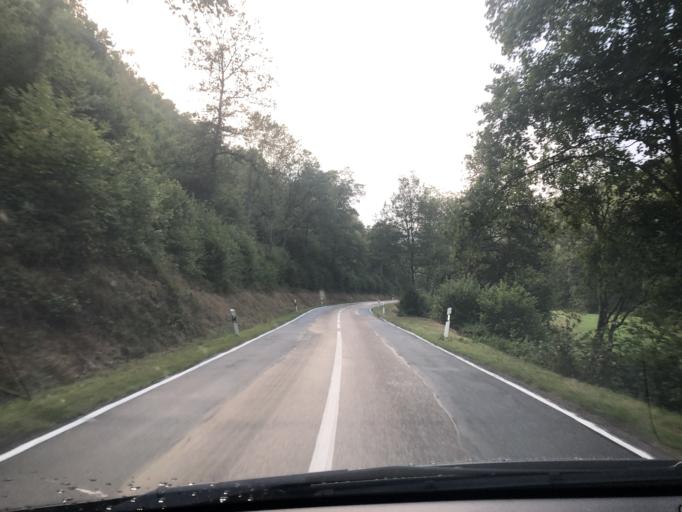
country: DE
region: Rheinland-Pfalz
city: Grimburg
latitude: 49.5987
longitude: 6.8780
